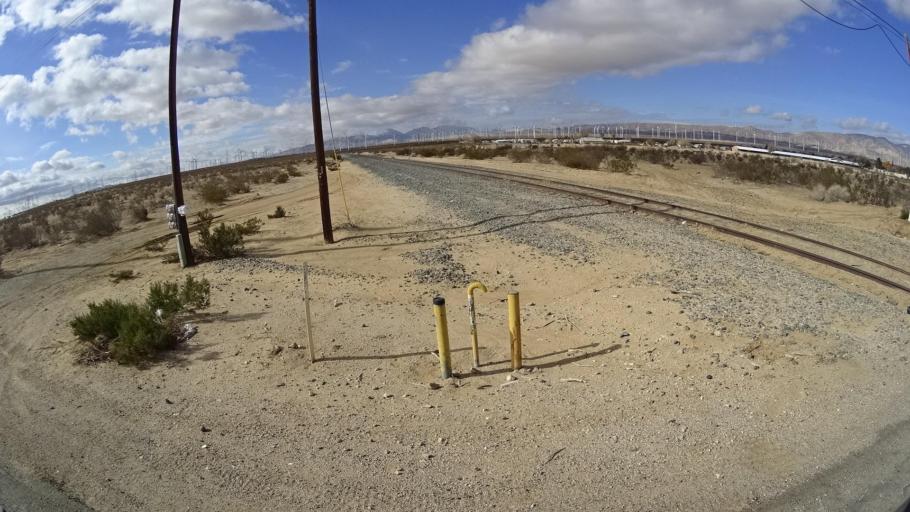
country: US
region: California
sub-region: Kern County
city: Mojave
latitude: 35.0462
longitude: -118.1846
